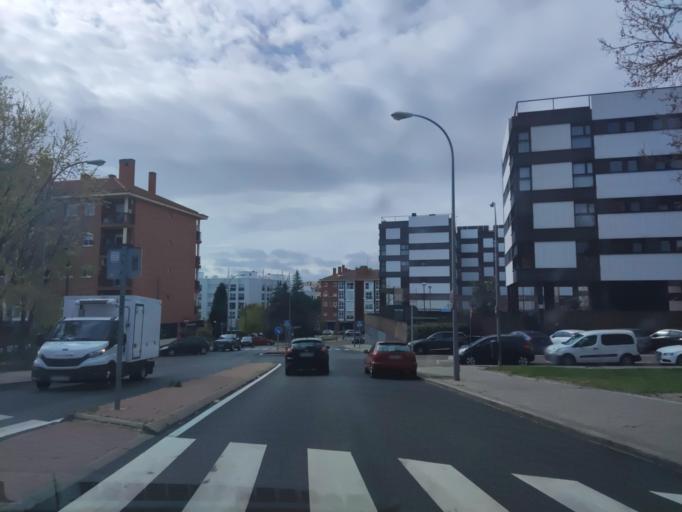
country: ES
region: Madrid
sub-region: Provincia de Madrid
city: Hortaleza
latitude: 40.4638
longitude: -3.6300
